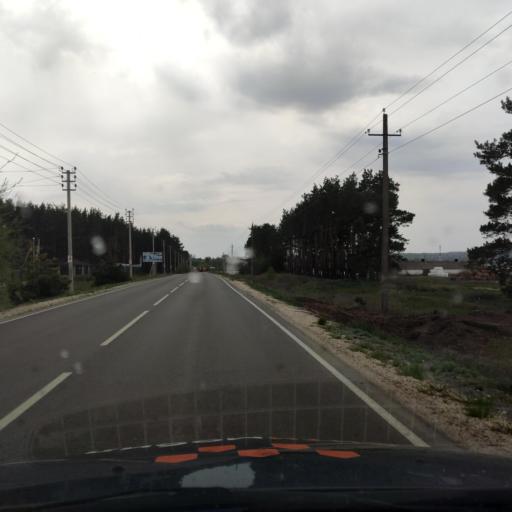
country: RU
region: Voronezj
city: Podgornoye
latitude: 51.8545
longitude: 39.1580
